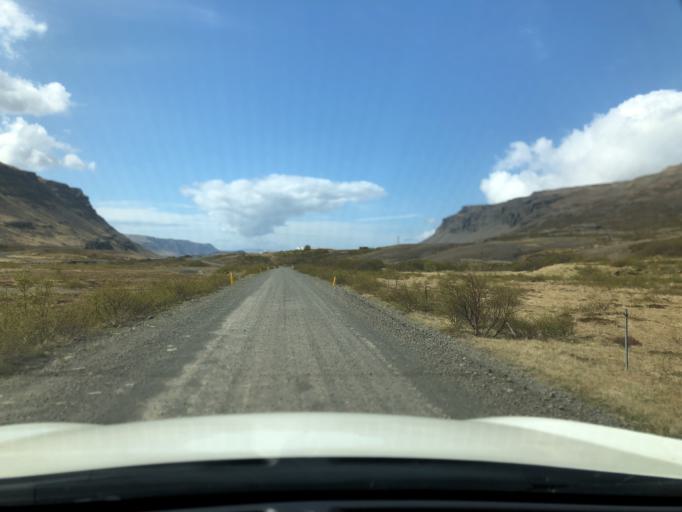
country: IS
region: South
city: Hveragerdi
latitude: 64.3857
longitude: -21.3331
